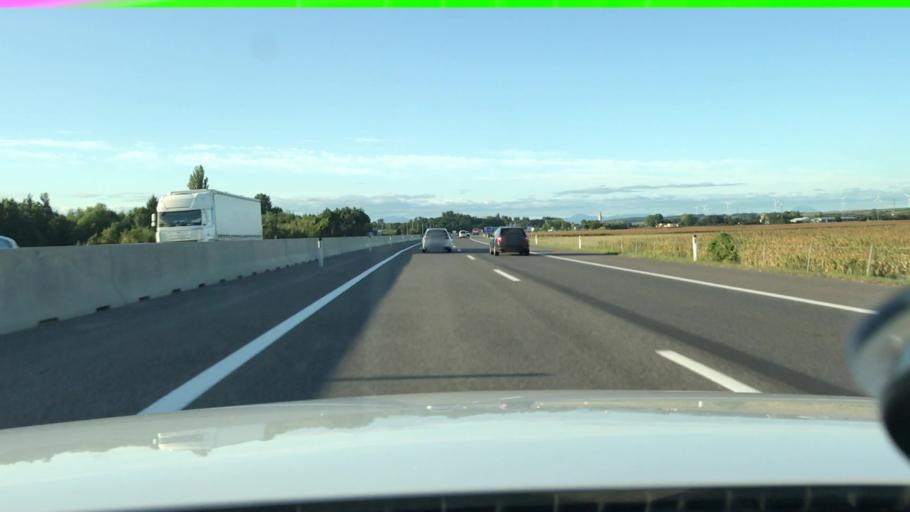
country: AT
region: Lower Austria
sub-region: Politischer Bezirk Sankt Polten
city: Traismauer
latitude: 48.3167
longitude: 15.7180
